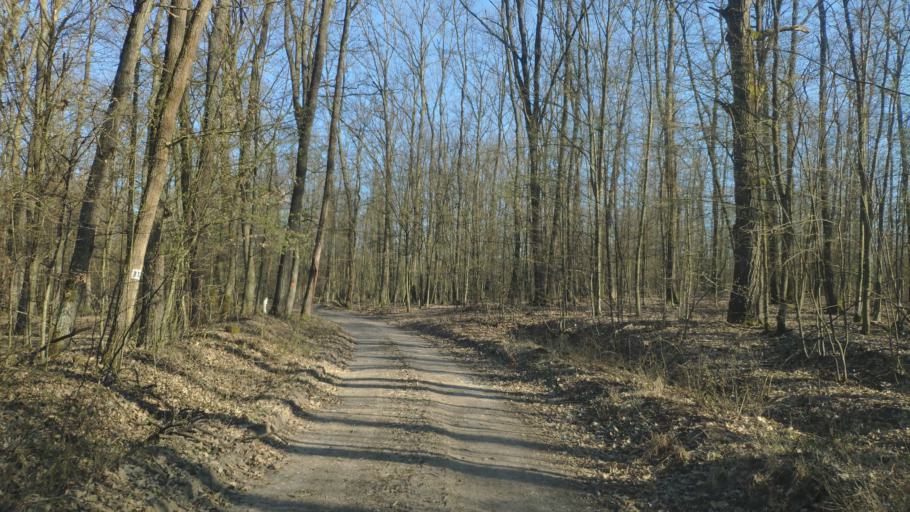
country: HU
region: Borsod-Abauj-Zemplen
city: Putnok
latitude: 48.5019
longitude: 20.2900
